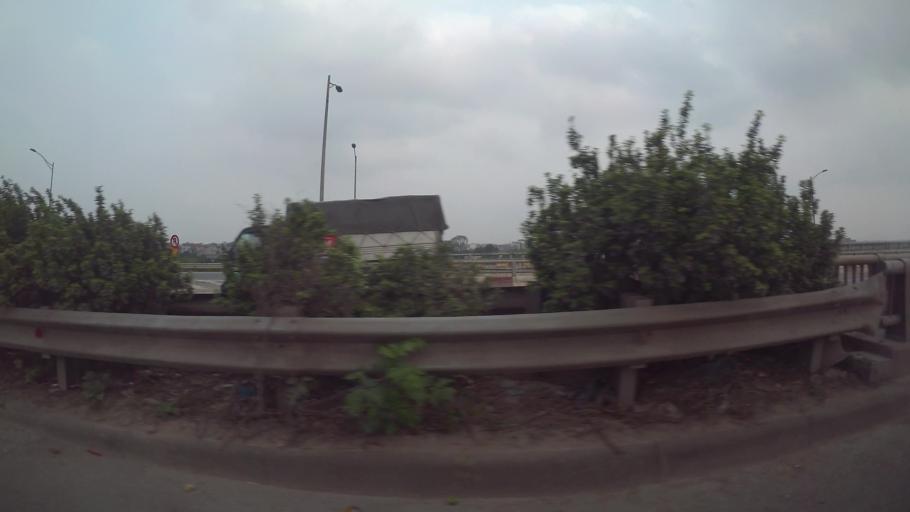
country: VN
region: Ha Noi
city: Trau Quy
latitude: 21.0166
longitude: 105.9211
